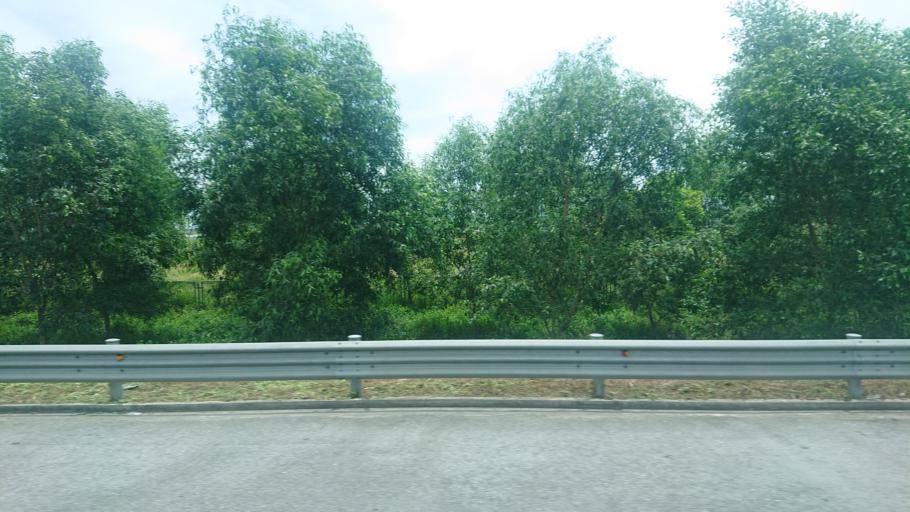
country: VN
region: Hai Phong
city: An Lao
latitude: 20.7979
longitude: 106.5401
